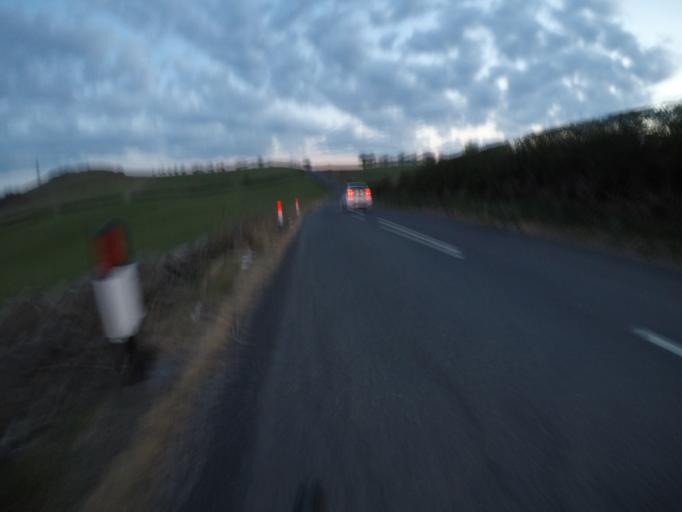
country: GB
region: Scotland
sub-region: South Ayrshire
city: Dundonald
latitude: 55.5643
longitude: -4.6029
